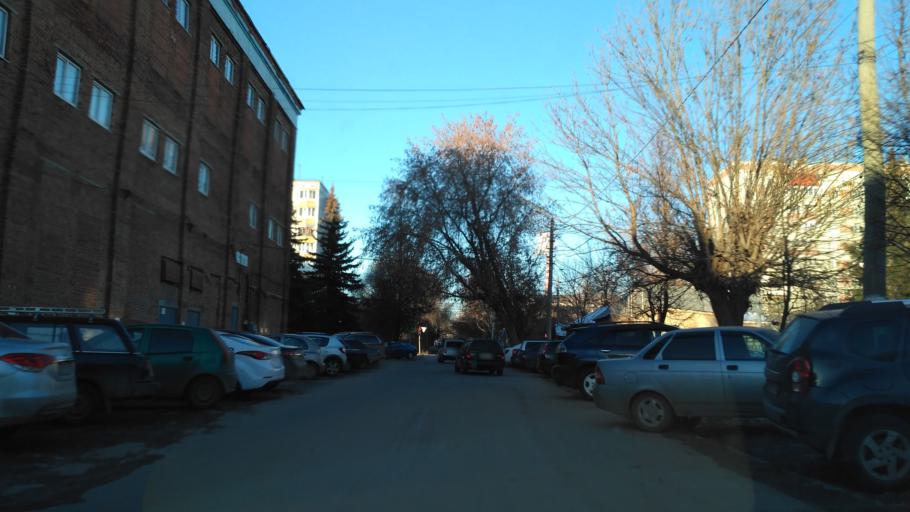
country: RU
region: Tula
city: Tula
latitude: 54.2067
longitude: 37.6080
